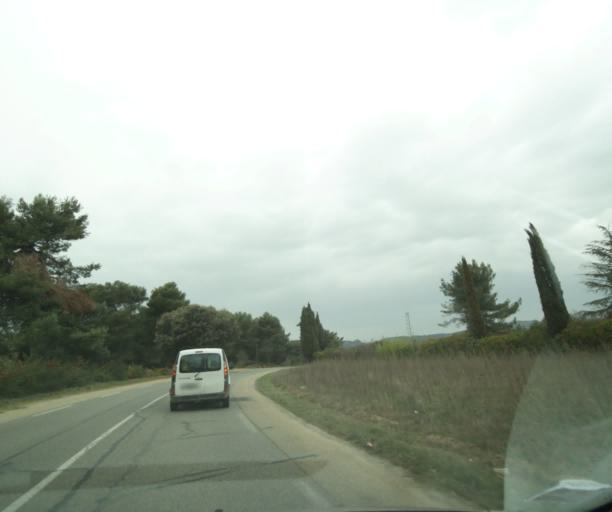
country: FR
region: Provence-Alpes-Cote d'Azur
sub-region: Departement des Bouches-du-Rhone
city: Peyrolles-en-Provence
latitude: 43.6437
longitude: 5.6066
